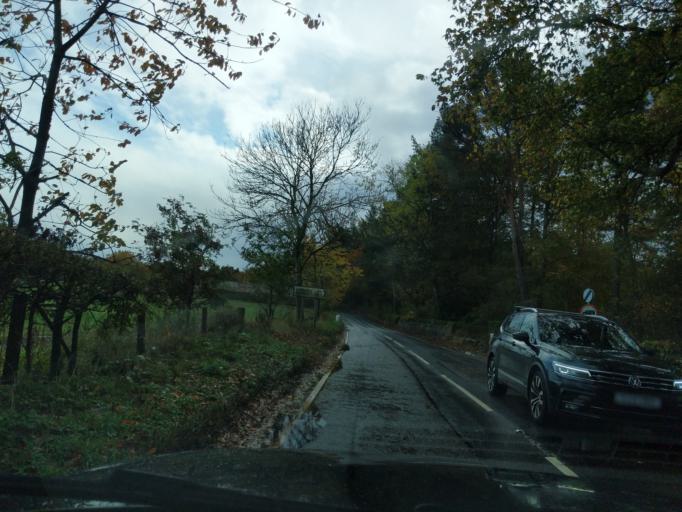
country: GB
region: Scotland
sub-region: Fife
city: Saint Andrews
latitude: 56.2939
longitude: -2.7525
